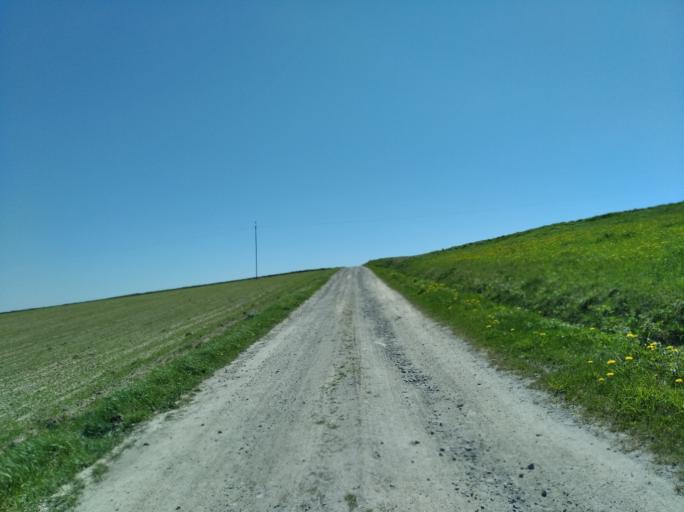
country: PL
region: Subcarpathian Voivodeship
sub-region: Powiat ropczycko-sedziszowski
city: Wielopole Skrzynskie
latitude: 49.9060
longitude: 21.5487
